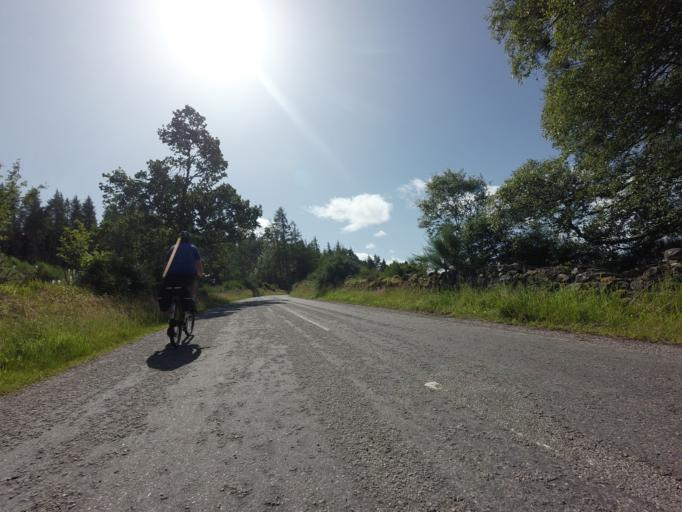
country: GB
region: Scotland
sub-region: Highland
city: Nairn
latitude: 57.5044
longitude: -3.9383
